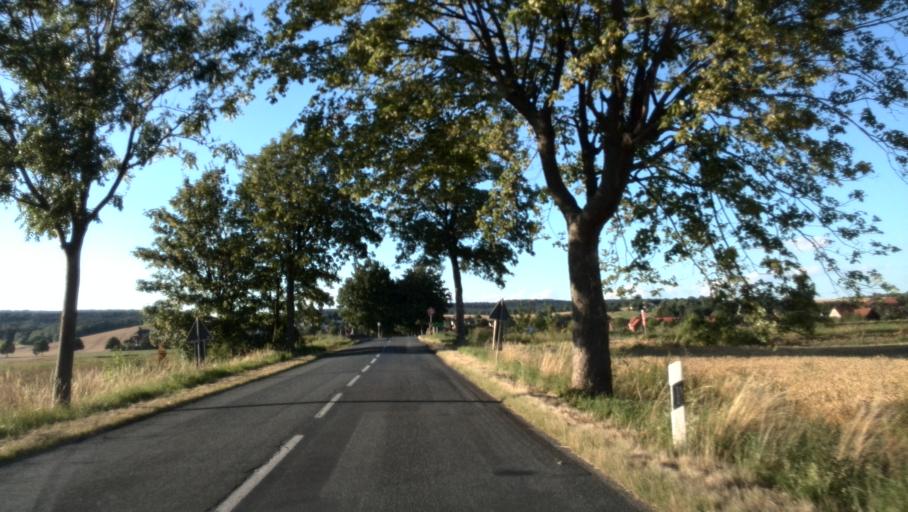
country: DE
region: Lower Saxony
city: Holle
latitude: 52.1003
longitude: 10.1002
